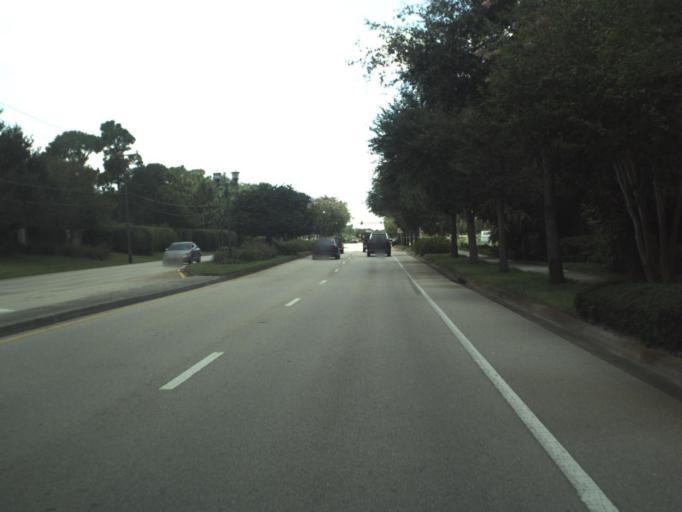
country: US
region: Florida
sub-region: Martin County
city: Palm City
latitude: 27.1620
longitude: -80.2374
